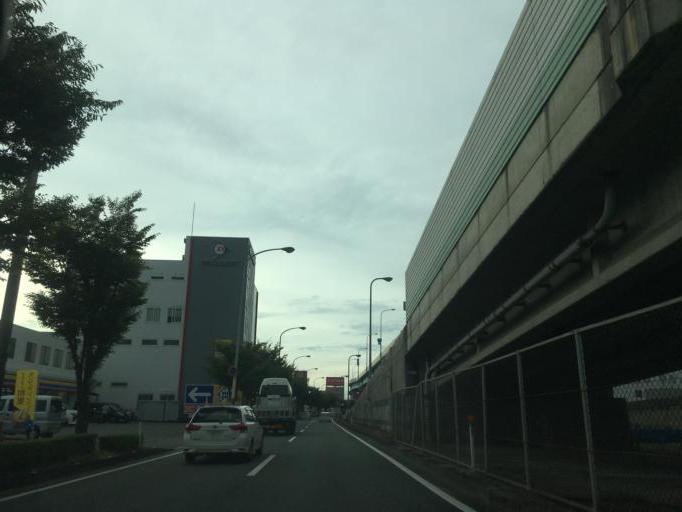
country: JP
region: Fukuoka
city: Fukuoka-shi
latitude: 33.5930
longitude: 130.4359
